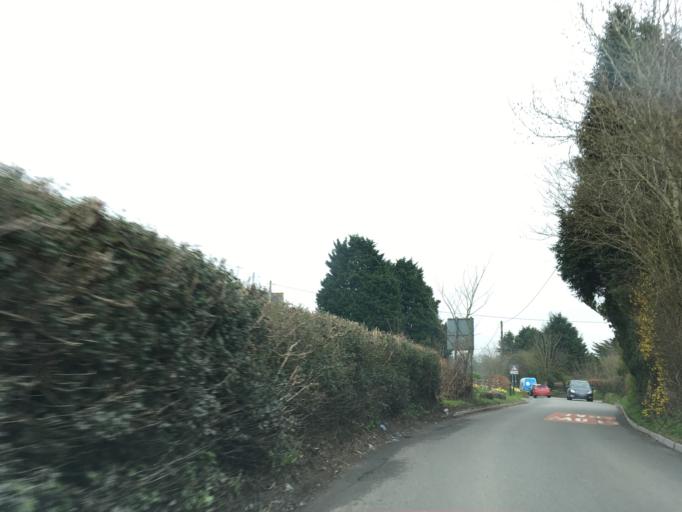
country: GB
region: Wales
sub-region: Caerphilly County Borough
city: Machen
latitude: 51.5408
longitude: -3.1606
